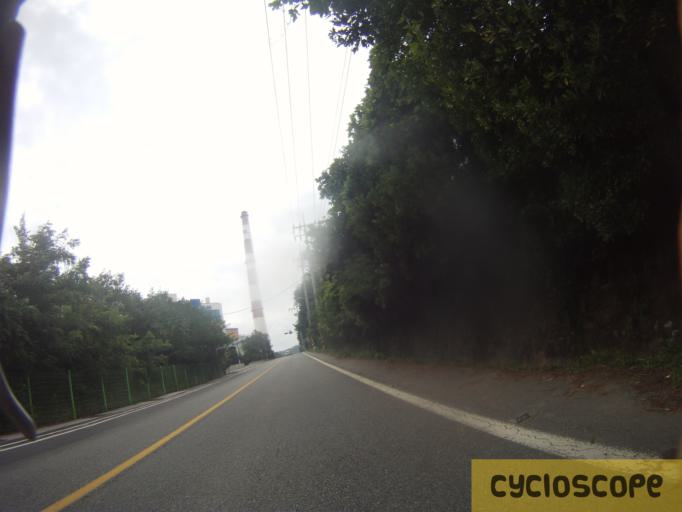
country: KR
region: Busan
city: Kijang
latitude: 35.2666
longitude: 129.2380
